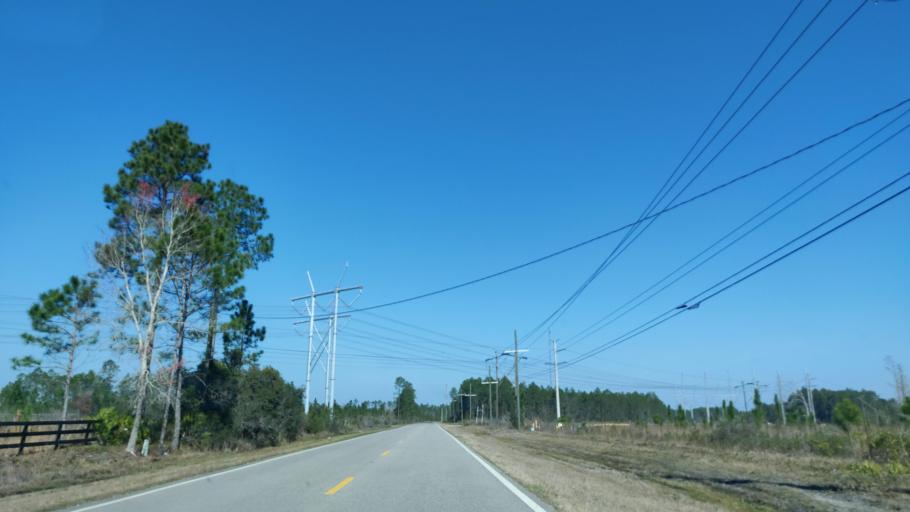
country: US
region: Florida
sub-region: Duval County
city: Baldwin
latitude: 30.2603
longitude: -81.9530
